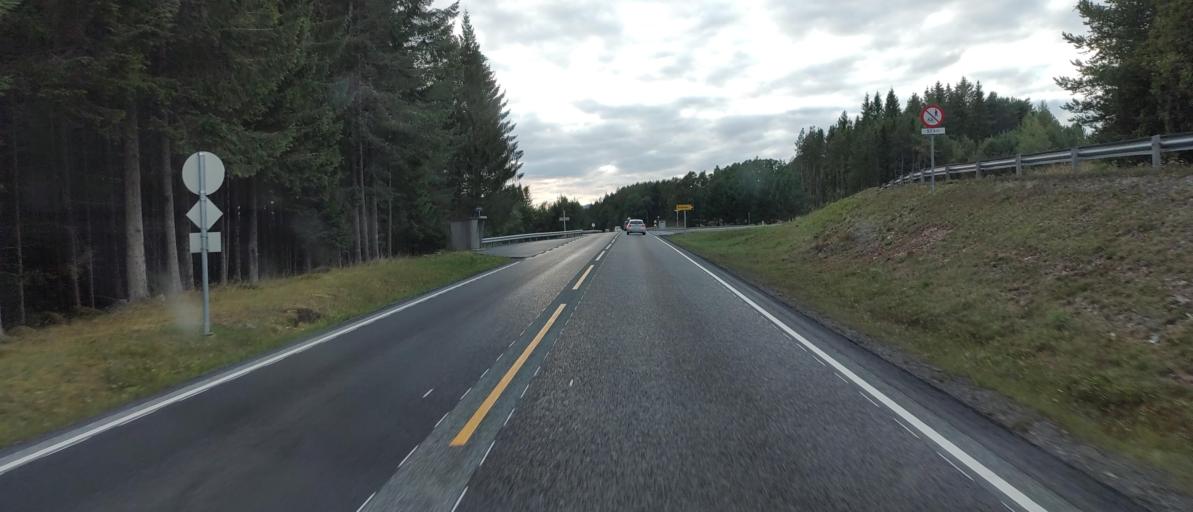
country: NO
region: More og Romsdal
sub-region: Molde
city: Hjelset
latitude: 62.7341
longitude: 7.3972
